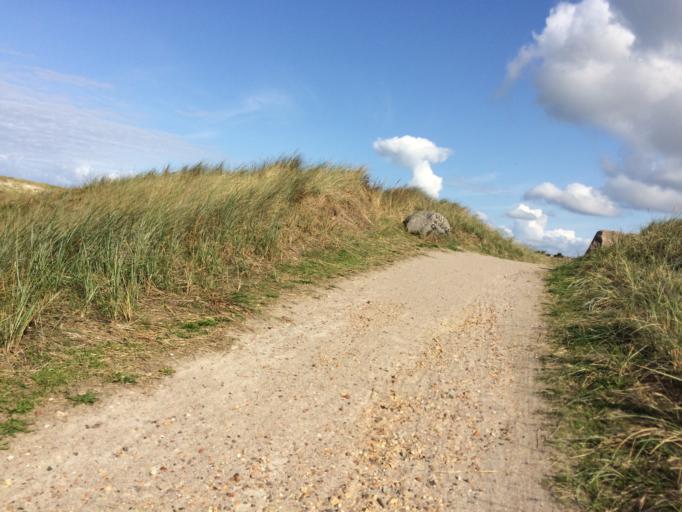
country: DK
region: Central Jutland
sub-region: Ringkobing-Skjern Kommune
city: Hvide Sande
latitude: 55.8981
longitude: 8.1599
